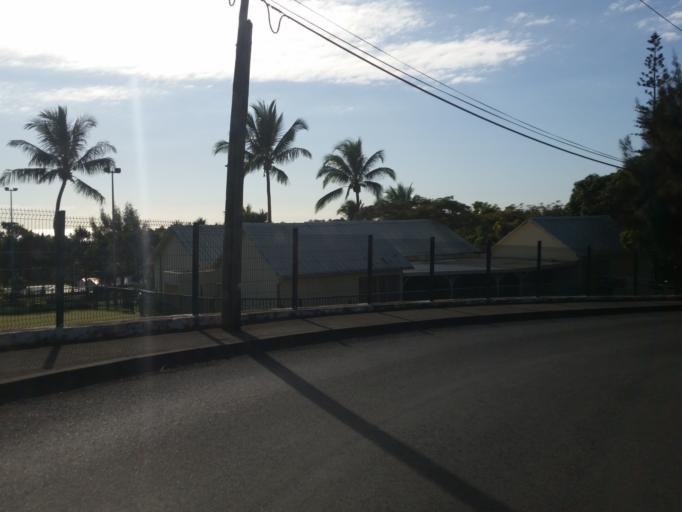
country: RE
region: Reunion
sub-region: Reunion
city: Sainte-Marie
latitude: -20.9104
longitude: 55.5037
